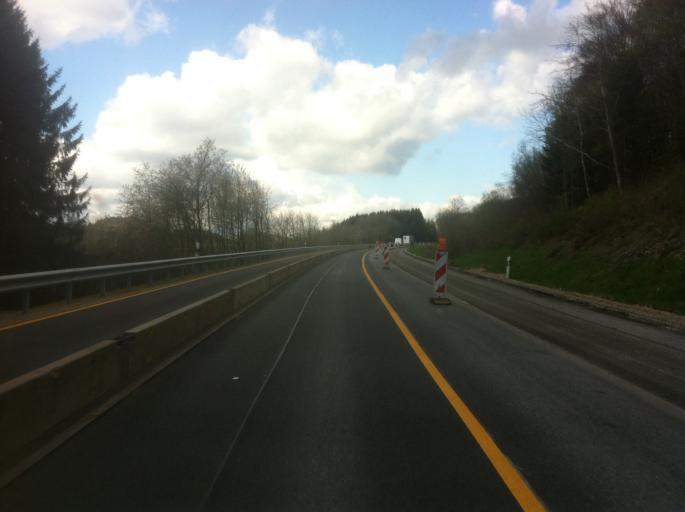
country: DE
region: Rheinland-Pfalz
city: Weinsheim
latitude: 50.2369
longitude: 6.4569
